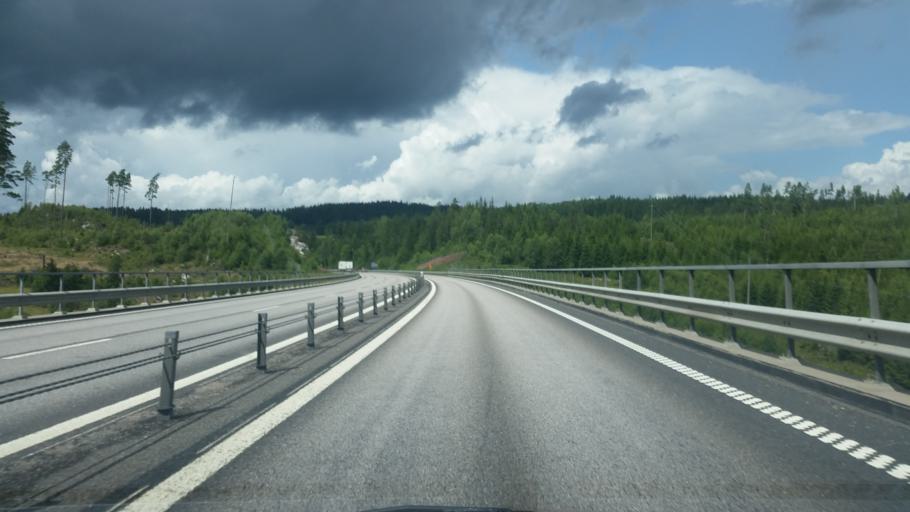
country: SE
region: Vaestra Goetaland
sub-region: Boras Kommun
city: Ganghester
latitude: 57.6687
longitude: 13.0292
